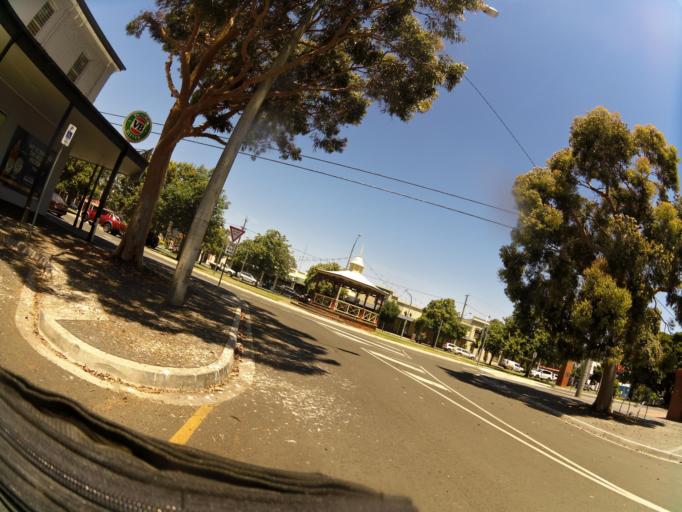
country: AU
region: Victoria
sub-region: Wellington
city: Sale
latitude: -37.9667
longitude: 146.9765
